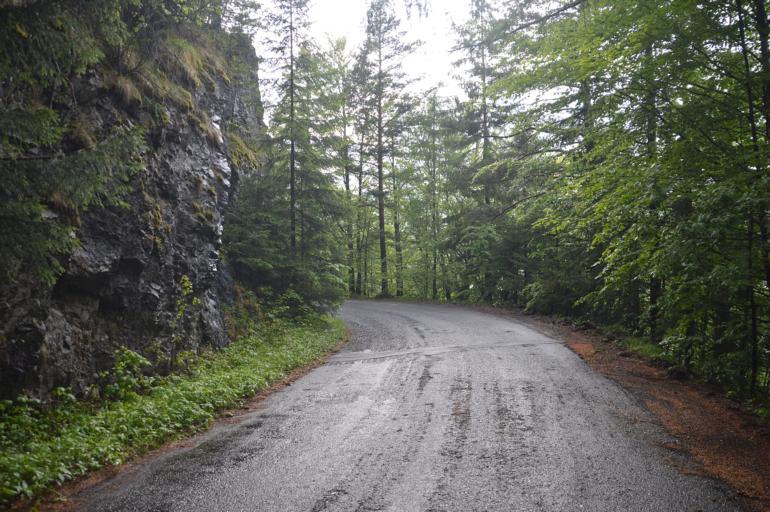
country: SK
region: Kosicky
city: Dobsina
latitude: 48.9096
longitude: 20.2933
